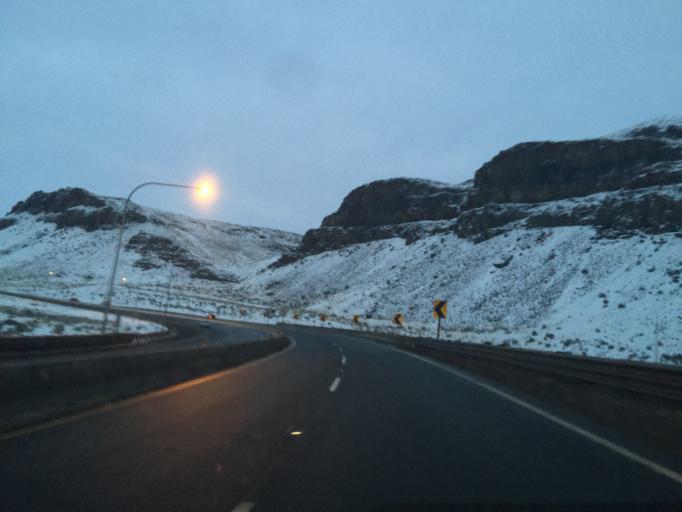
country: US
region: Washington
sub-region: Grant County
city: Mattawa
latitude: 46.9451
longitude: -119.9617
